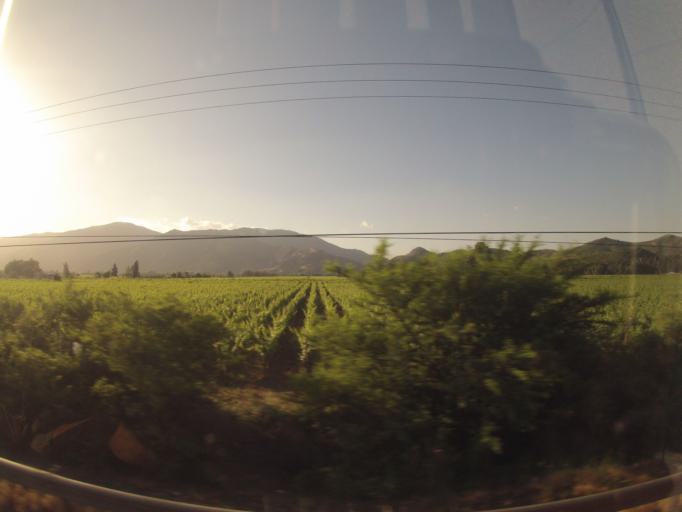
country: CL
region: O'Higgins
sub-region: Provincia de Cachapoal
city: Rengo
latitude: -34.5382
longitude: -70.9452
